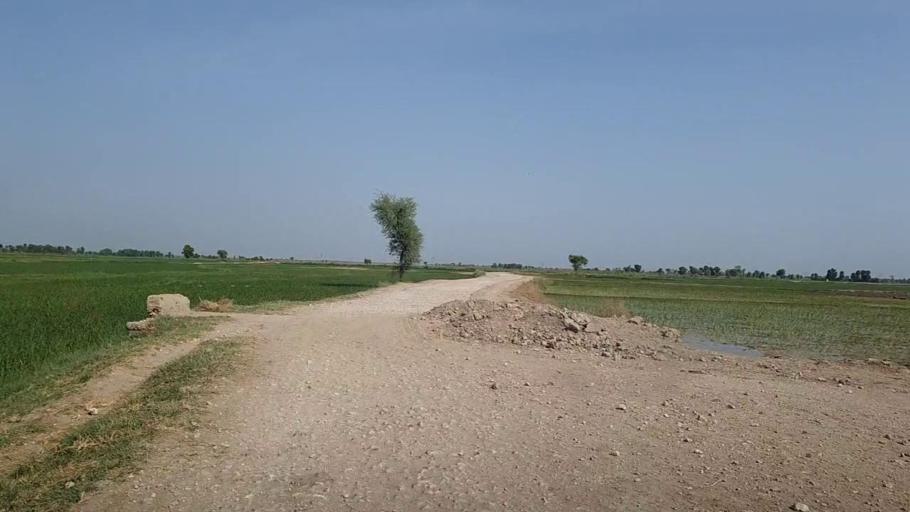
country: PK
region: Sindh
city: Mehar
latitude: 27.1131
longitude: 67.8455
